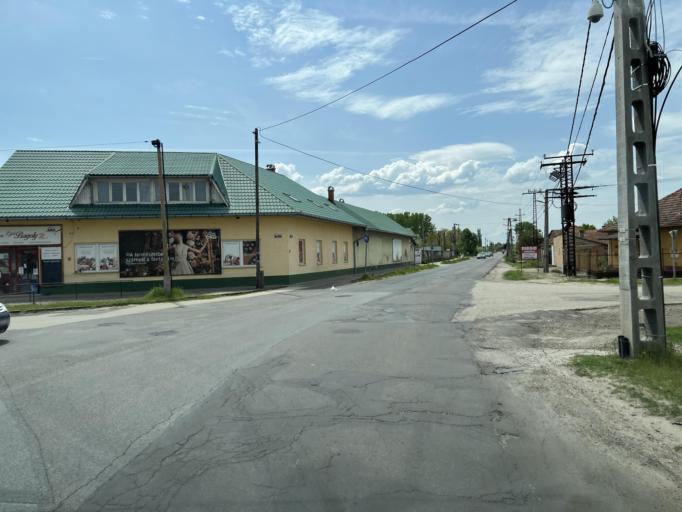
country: HU
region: Pest
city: Cegled
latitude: 47.1645
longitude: 19.7821
